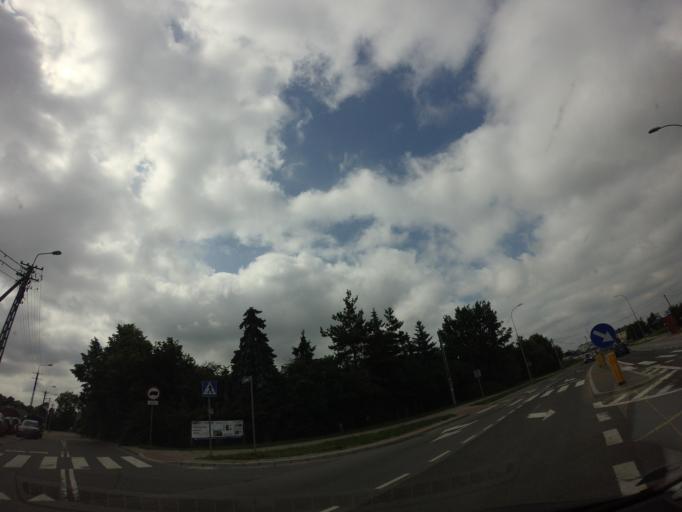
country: PL
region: Podlasie
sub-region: Bialystok
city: Bialystok
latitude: 53.1243
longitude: 23.2279
